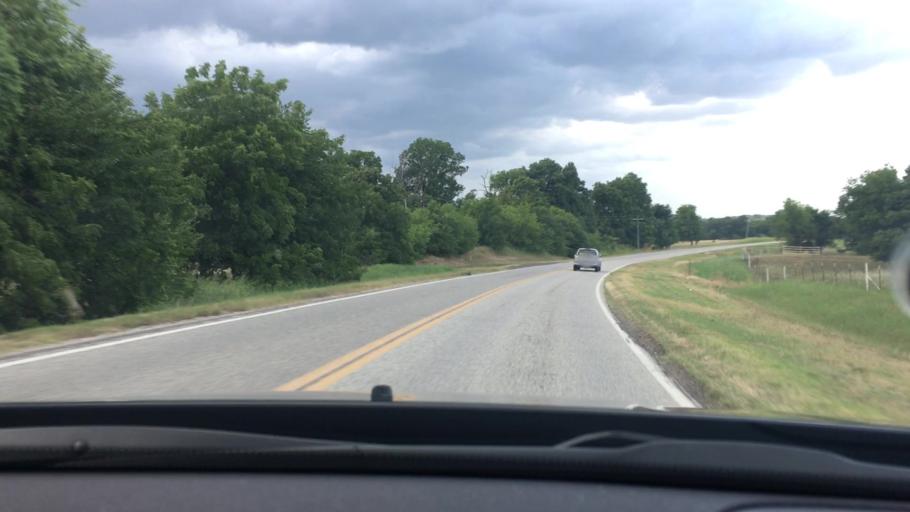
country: US
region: Oklahoma
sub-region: Pontotoc County
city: Ada
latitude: 34.5801
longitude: -96.6342
